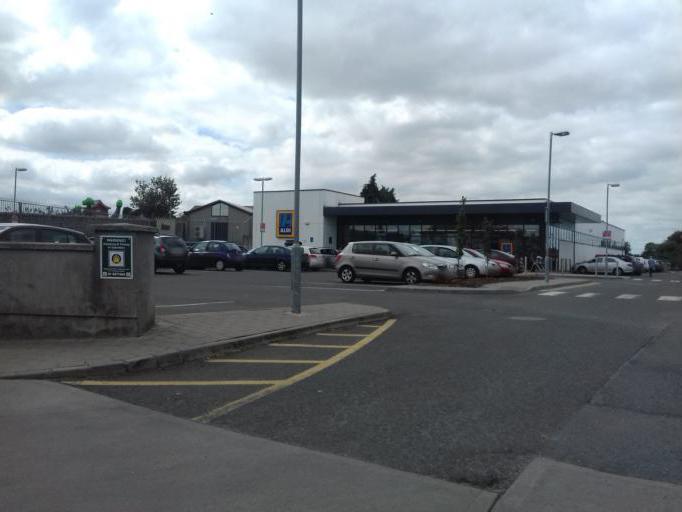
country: IE
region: Leinster
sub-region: County Carlow
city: Tullow
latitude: 52.8042
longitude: -6.7332
